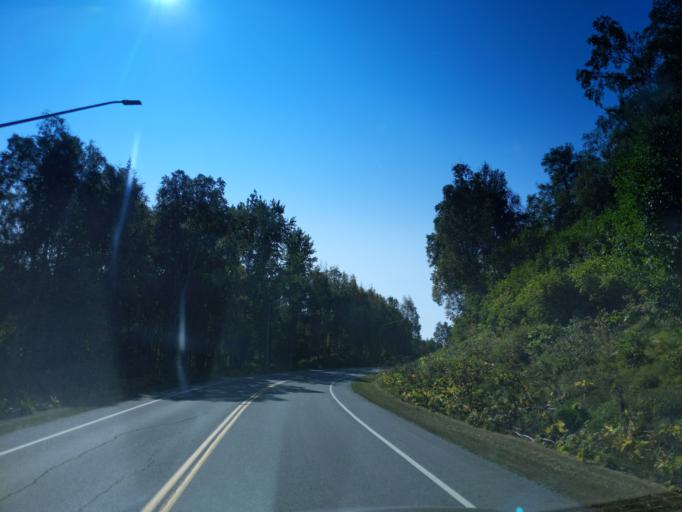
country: US
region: Alaska
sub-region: Anchorage Municipality
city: Anchorage
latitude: 61.1573
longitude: -150.0159
